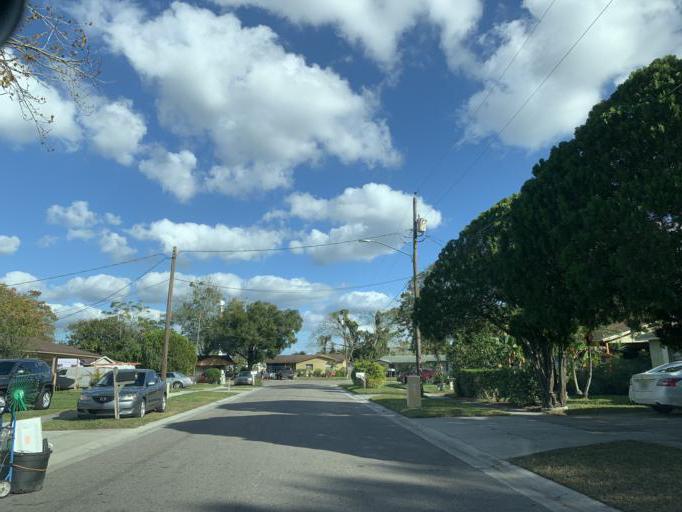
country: US
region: Florida
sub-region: Orange County
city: Eatonville
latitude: 28.6119
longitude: -81.3913
